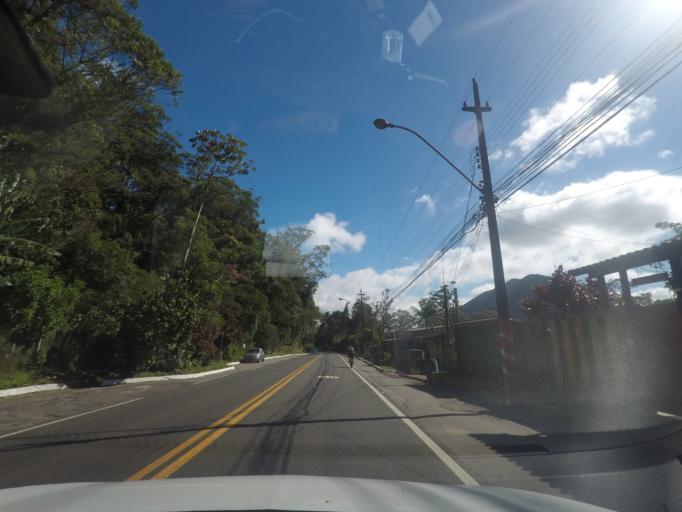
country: BR
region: Rio de Janeiro
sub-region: Teresopolis
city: Teresopolis
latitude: -22.4539
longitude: -42.9834
